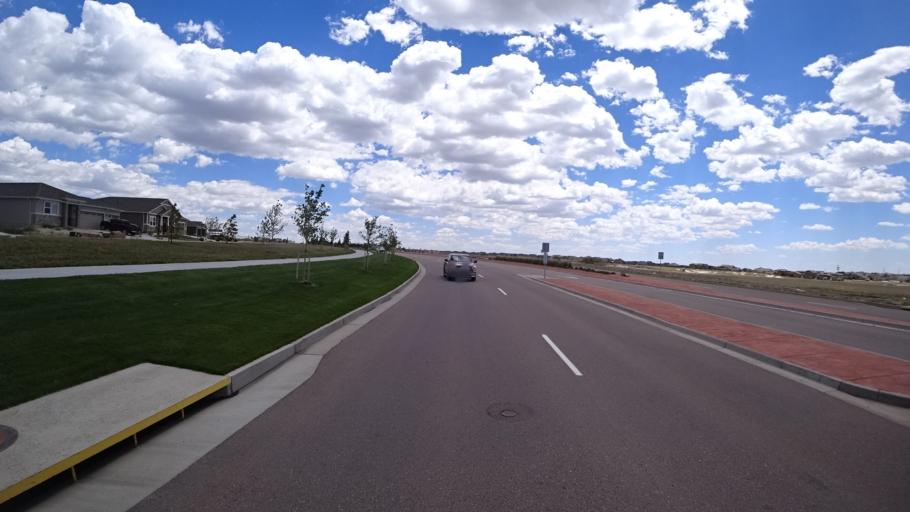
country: US
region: Colorado
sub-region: El Paso County
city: Black Forest
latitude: 38.9584
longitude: -104.7049
